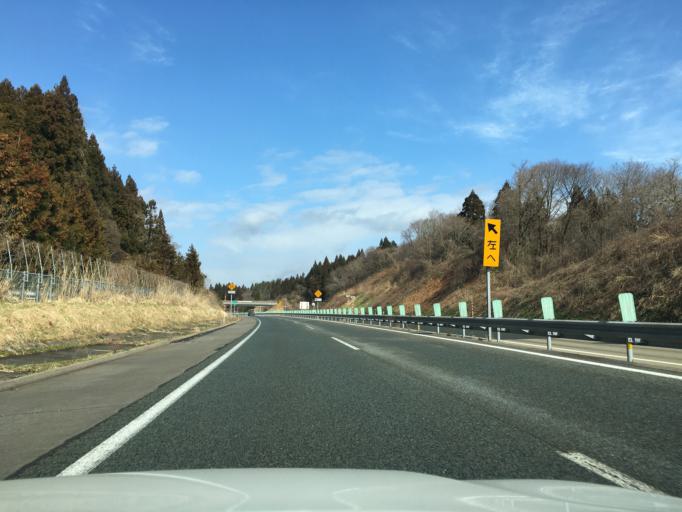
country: JP
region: Akita
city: Akita
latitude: 39.7260
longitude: 140.1807
